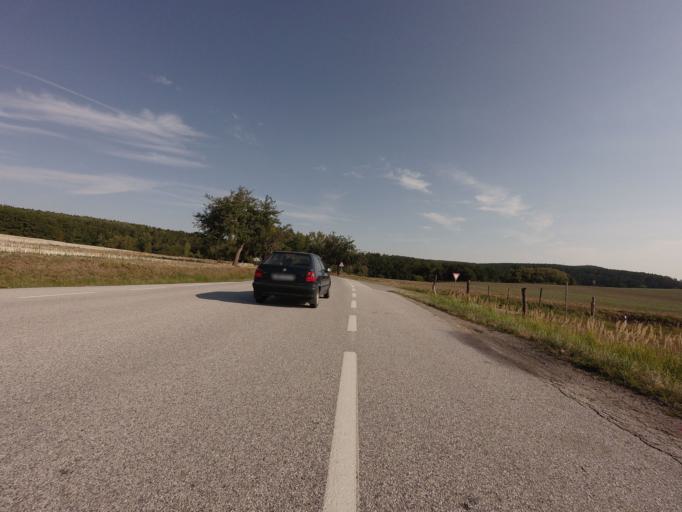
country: CZ
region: Jihocesky
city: Tyn nad Vltavou
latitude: 49.2610
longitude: 14.4132
